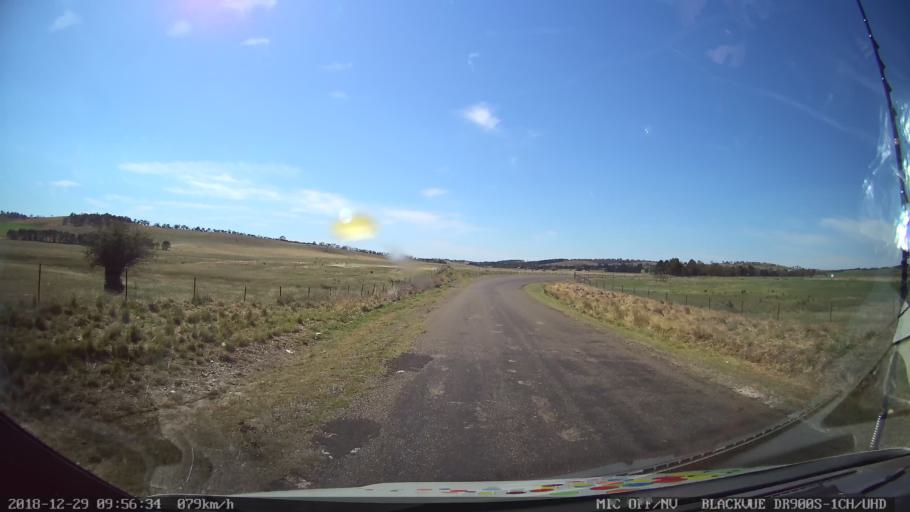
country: AU
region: New South Wales
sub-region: Goulburn Mulwaree
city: Goulburn
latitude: -34.7779
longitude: 149.4811
